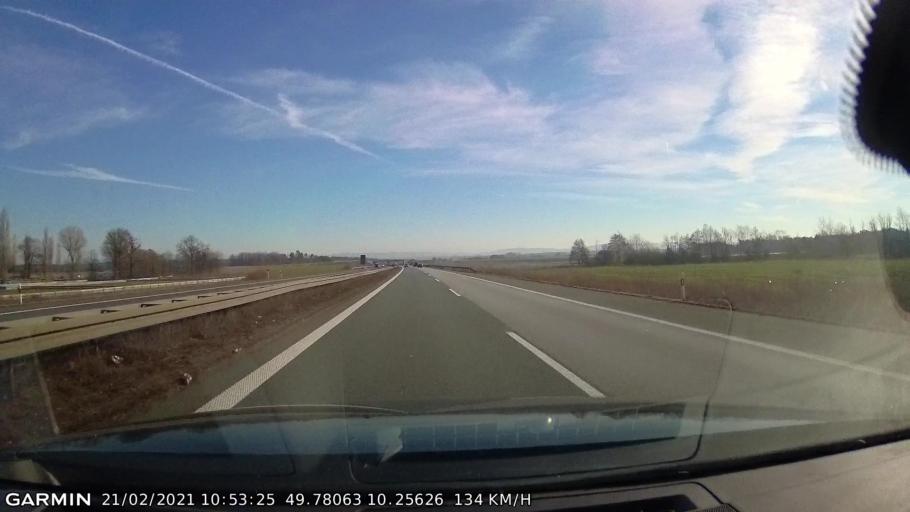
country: DE
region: Bavaria
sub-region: Regierungsbezirk Unterfranken
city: Grosslangheim
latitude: 49.7809
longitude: 10.2566
